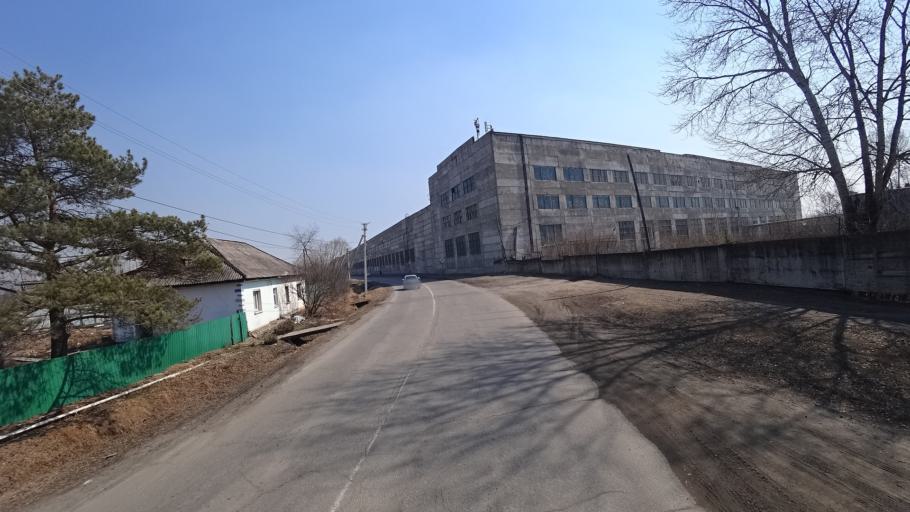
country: RU
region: Amur
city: Novobureyskiy
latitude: 49.7925
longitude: 129.8574
